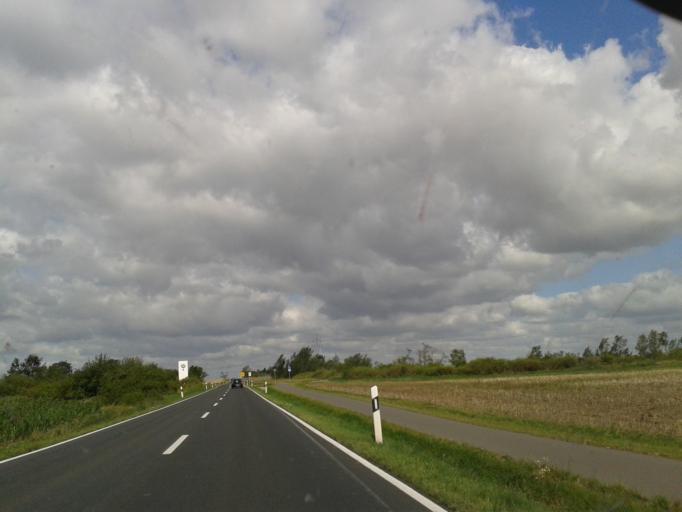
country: DE
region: Saxony-Anhalt
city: Lieskau
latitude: 51.5152
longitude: 11.8679
